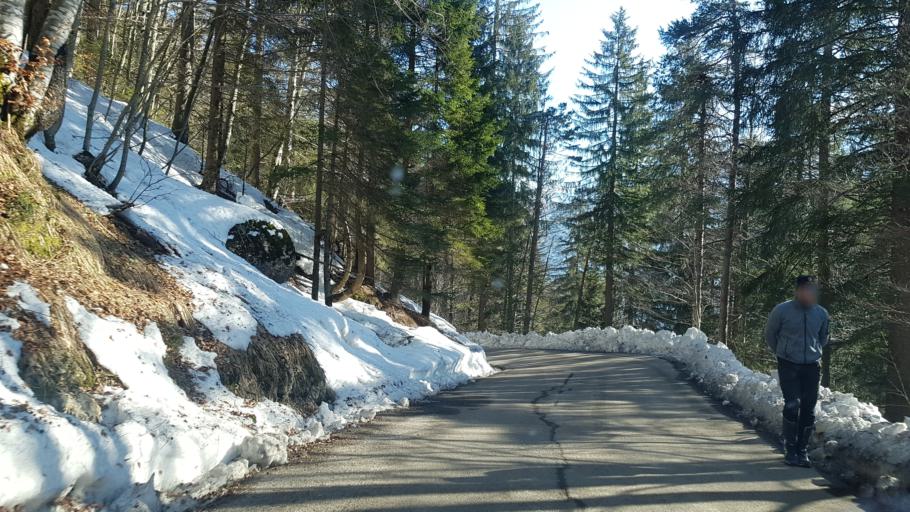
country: IT
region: Friuli Venezia Giulia
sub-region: Provincia di Udine
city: Malborghetto
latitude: 46.5171
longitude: 13.4708
